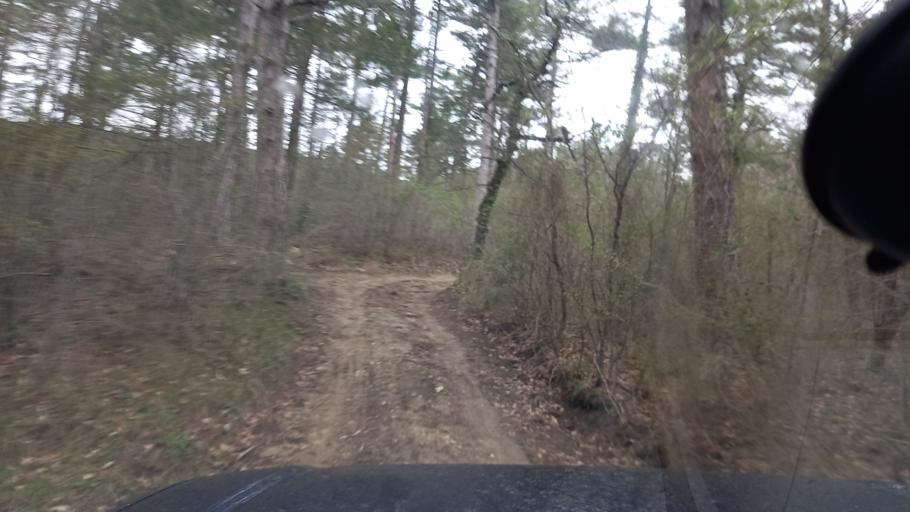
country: RU
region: Krasnodarskiy
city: Arkhipo-Osipovka
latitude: 44.3707
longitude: 38.4725
